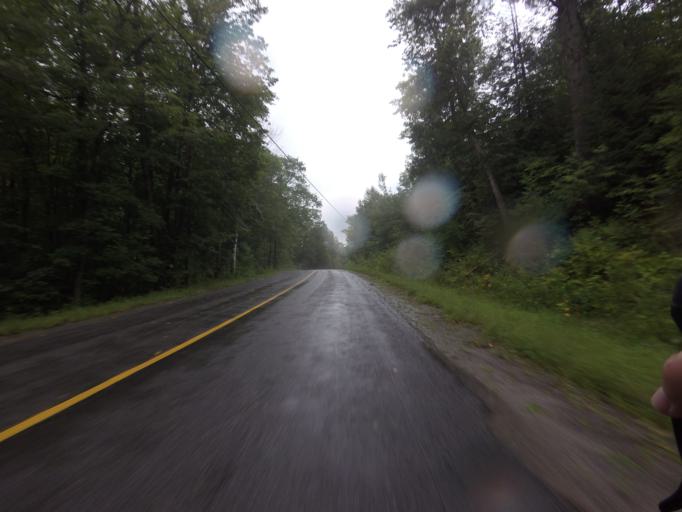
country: CA
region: Ontario
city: Perth
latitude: 45.0589
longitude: -76.6161
